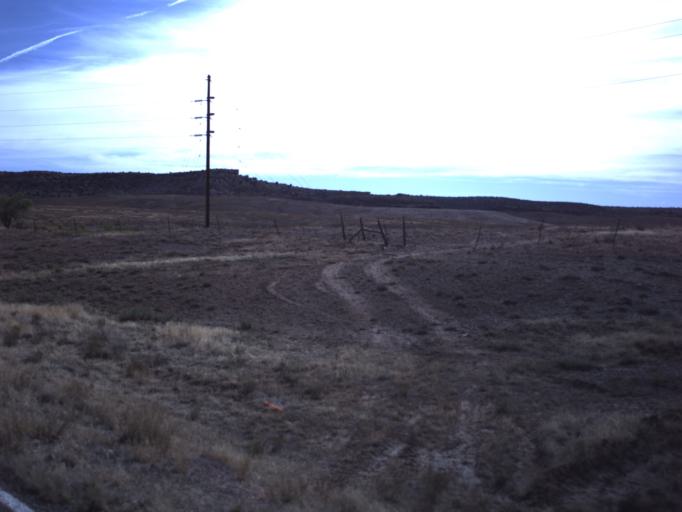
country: US
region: Utah
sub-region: San Juan County
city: Blanding
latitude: 37.4200
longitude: -109.4224
